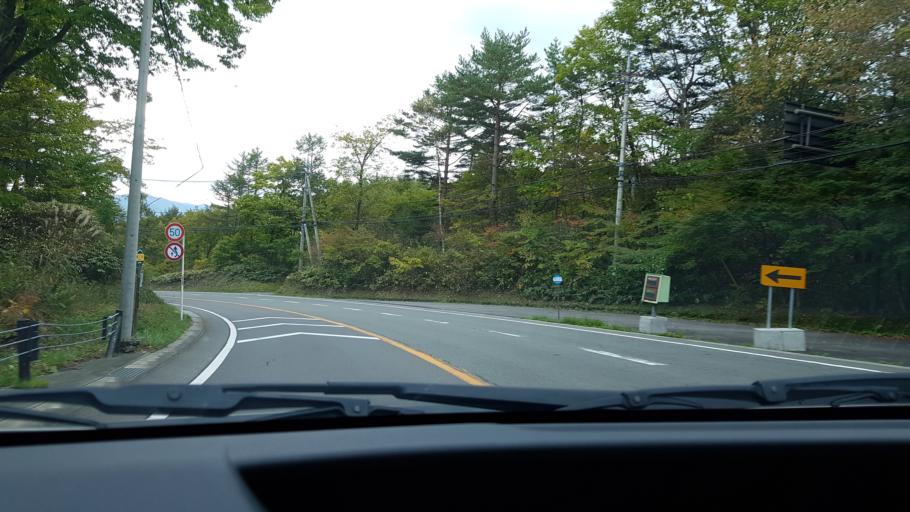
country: JP
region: Gunma
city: Nakanojomachi
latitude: 36.6042
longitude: 138.5836
